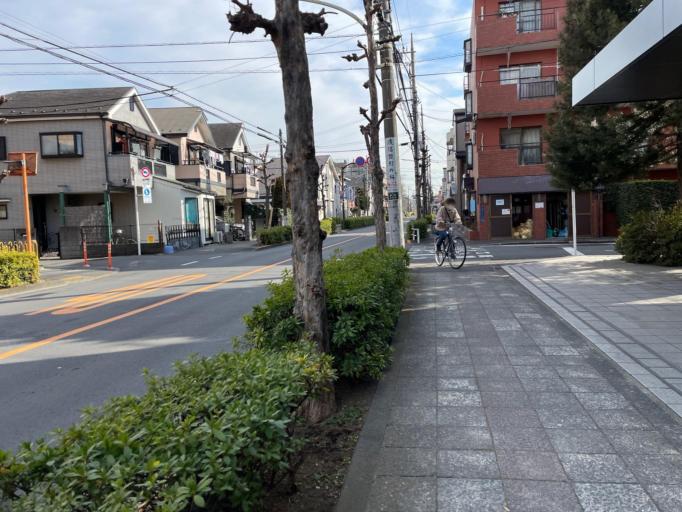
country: JP
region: Tokyo
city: Nishi-Tokyo-shi
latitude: 35.7054
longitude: 139.5146
